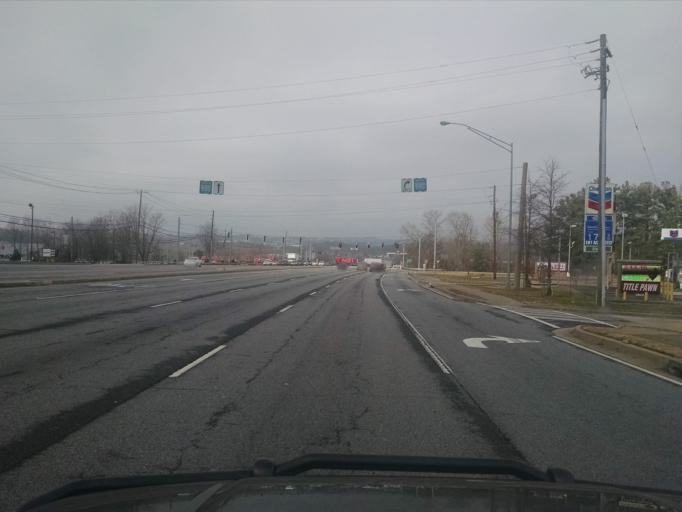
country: US
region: Georgia
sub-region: Gwinnett County
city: Buford
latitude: 34.0858
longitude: -83.9912
